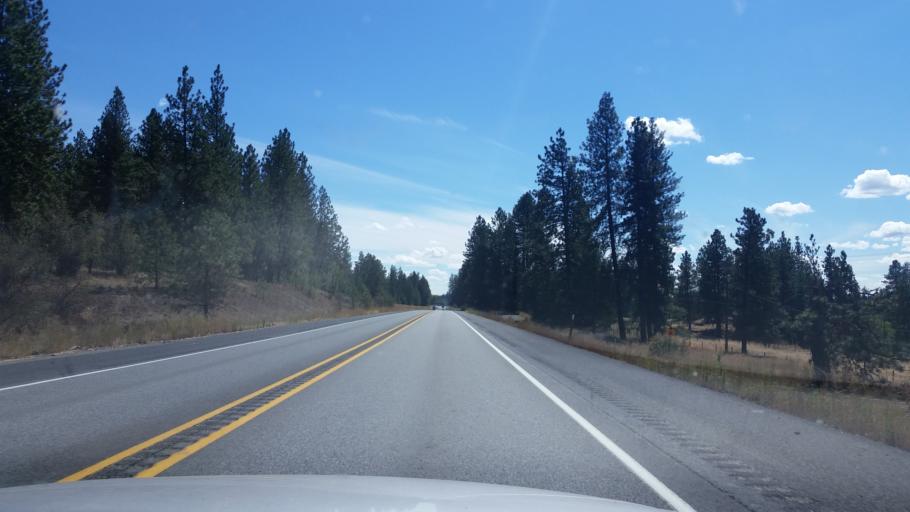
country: US
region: Washington
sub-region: Spokane County
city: Cheney
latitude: 47.5401
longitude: -117.5796
